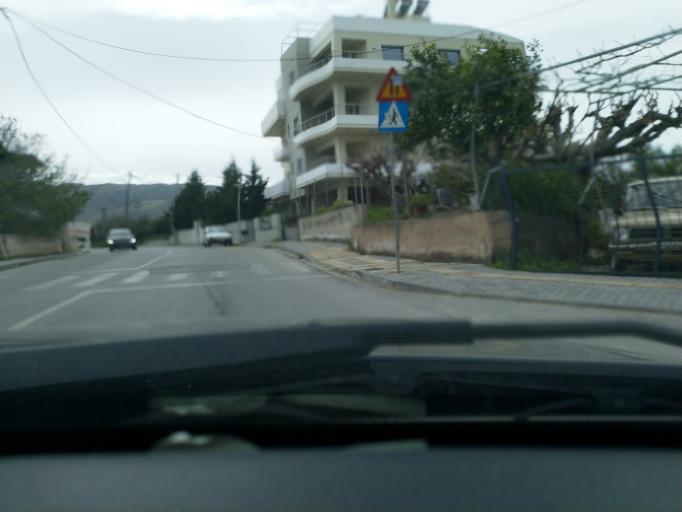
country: GR
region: Crete
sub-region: Nomos Chanias
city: Chania
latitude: 35.4994
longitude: 24.0215
